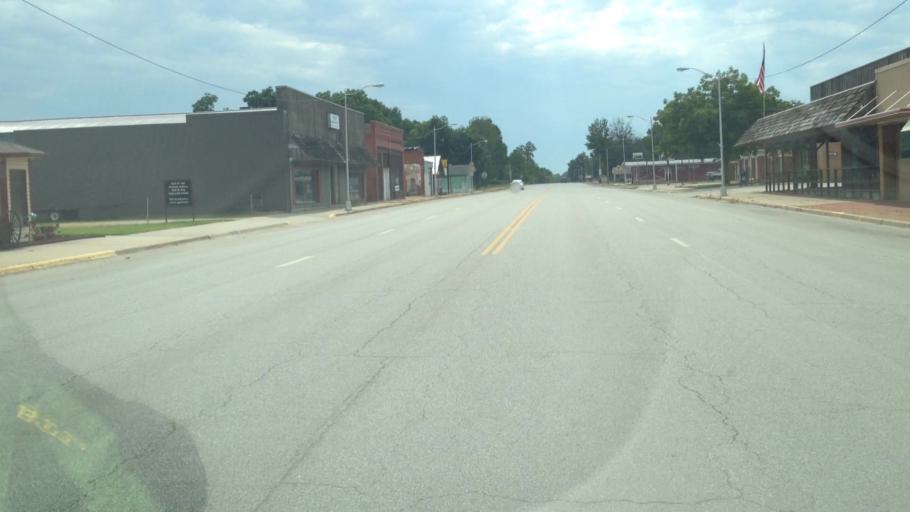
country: US
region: Kansas
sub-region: Labette County
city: Chetopa
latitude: 37.0369
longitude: -95.0894
